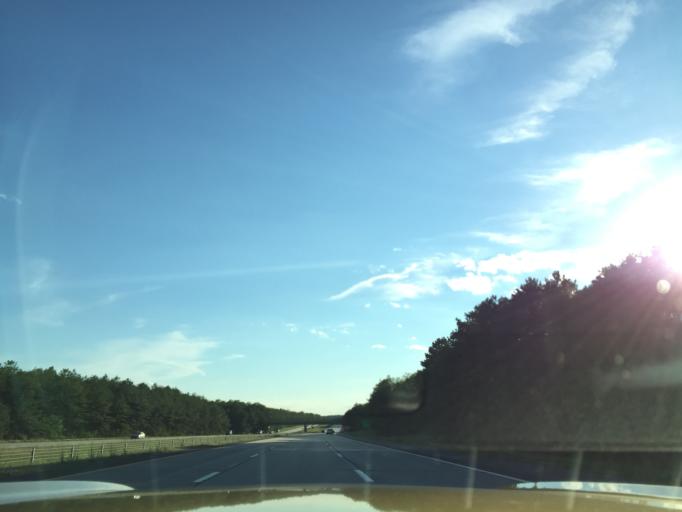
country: US
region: New York
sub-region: Suffolk County
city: Manorville
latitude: 40.8790
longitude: -72.7765
